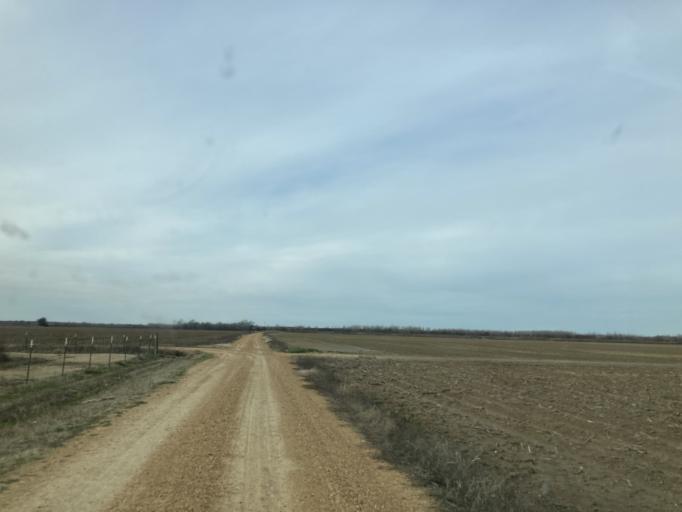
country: US
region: Mississippi
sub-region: Humphreys County
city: Belzoni
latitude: 33.1235
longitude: -90.6190
